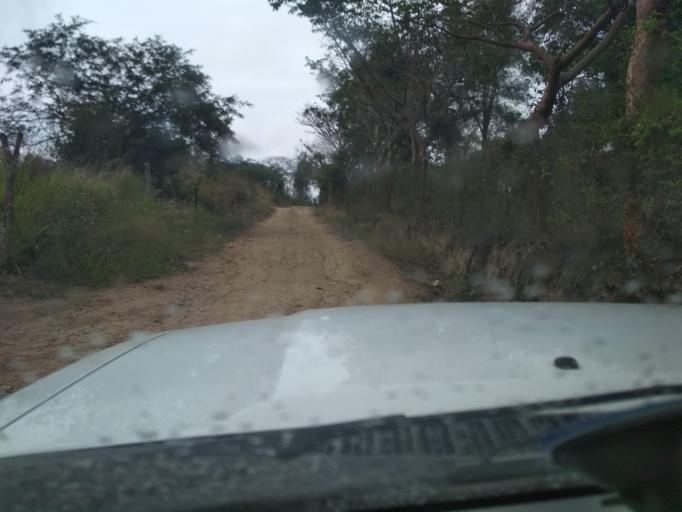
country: MX
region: Veracruz
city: El Castillo
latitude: 19.5371
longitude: -96.8270
